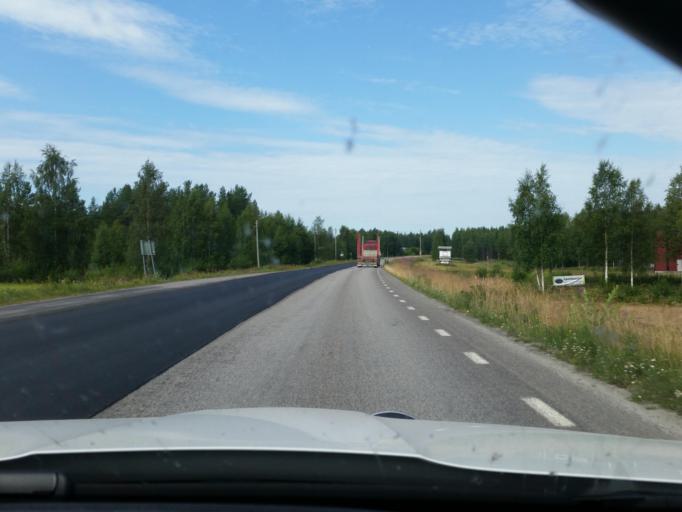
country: SE
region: Norrbotten
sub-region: Alvsbyns Kommun
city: AElvsbyn
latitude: 65.6936
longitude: 20.6640
